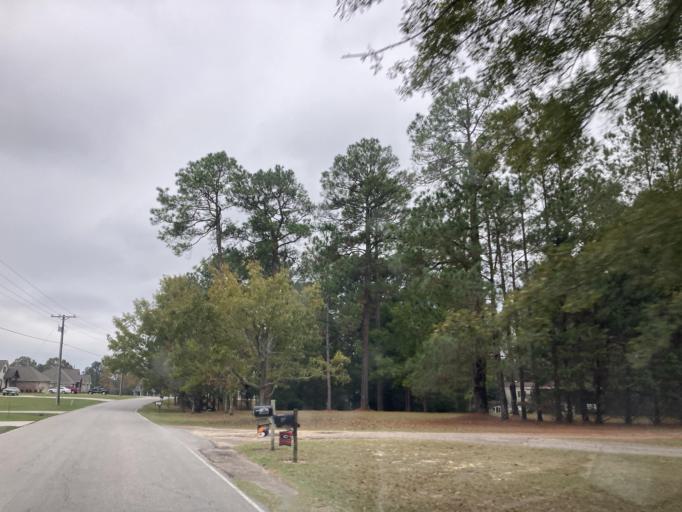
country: US
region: Mississippi
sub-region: Lamar County
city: Purvis
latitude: 31.1491
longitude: -89.4326
